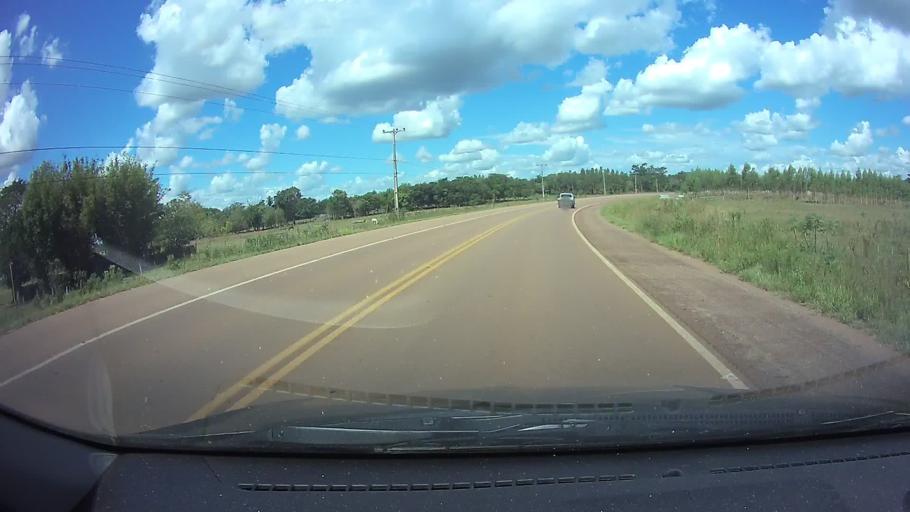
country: PY
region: Paraguari
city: La Colmena
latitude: -25.9135
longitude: -56.7127
